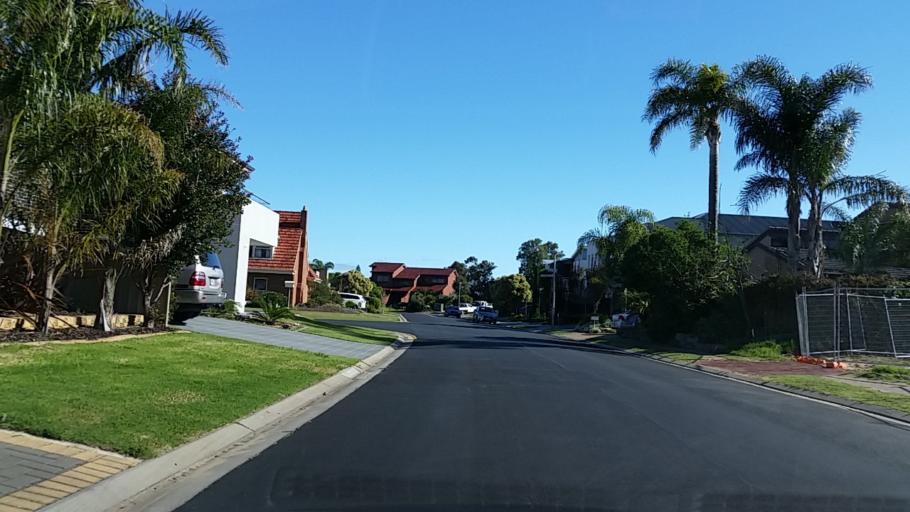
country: AU
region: South Australia
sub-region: Charles Sturt
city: West Lakes Shore
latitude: -34.8700
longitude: 138.4871
